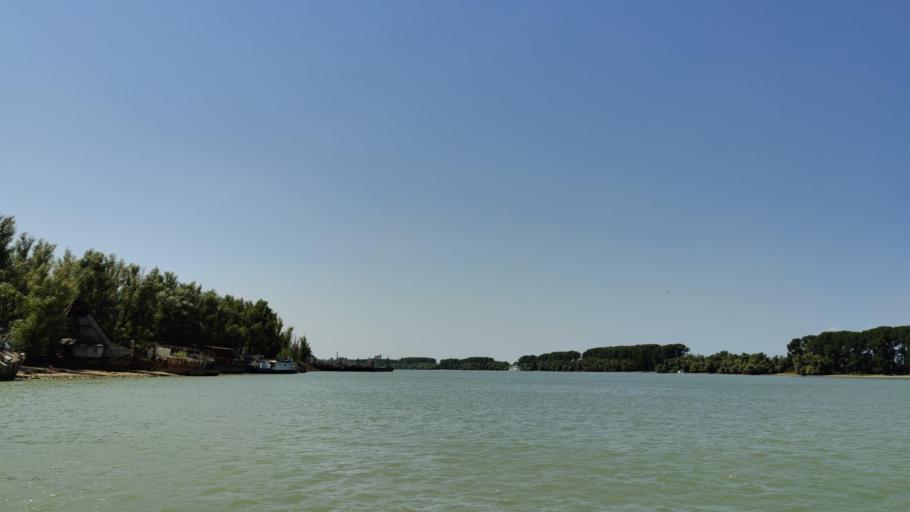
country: RO
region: Tulcea
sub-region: Municipiul Tulcea
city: Tulcea
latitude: 45.2018
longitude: 28.8398
